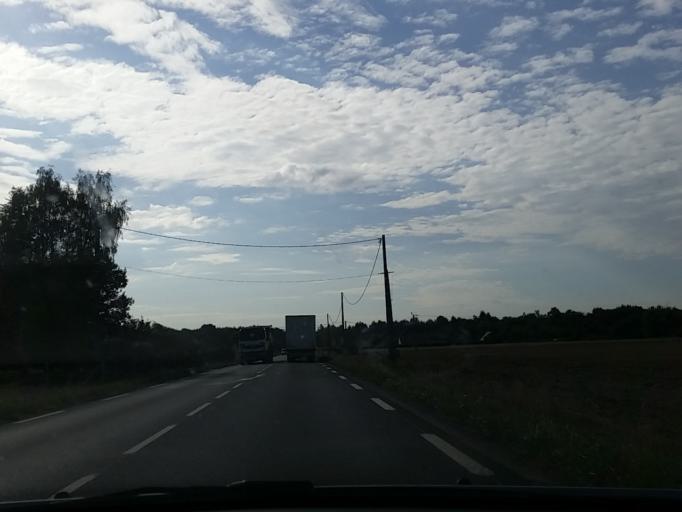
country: FR
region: Centre
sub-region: Departement du Loir-et-Cher
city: Pruniers-en-Sologne
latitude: 47.3796
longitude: 1.6834
